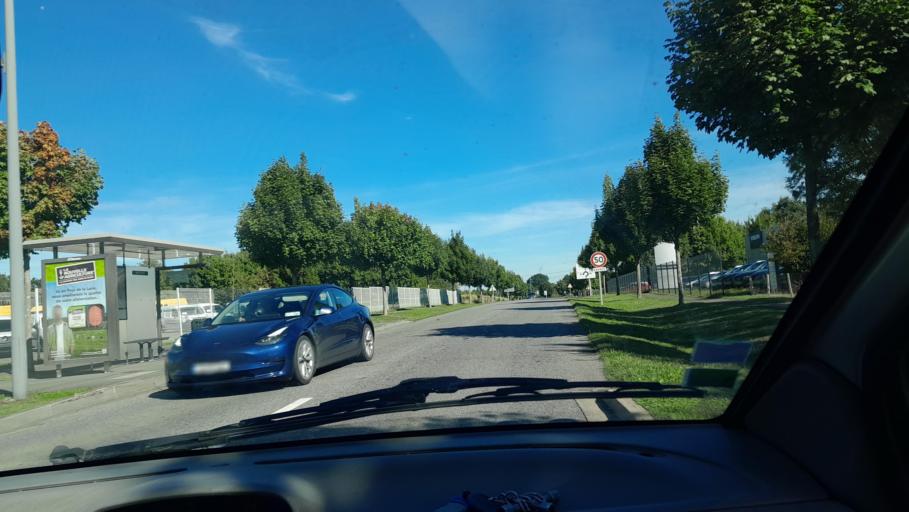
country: FR
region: Pays de la Loire
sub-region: Departement de la Mayenne
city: Saint-Berthevin
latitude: 48.0737
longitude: -0.8090
